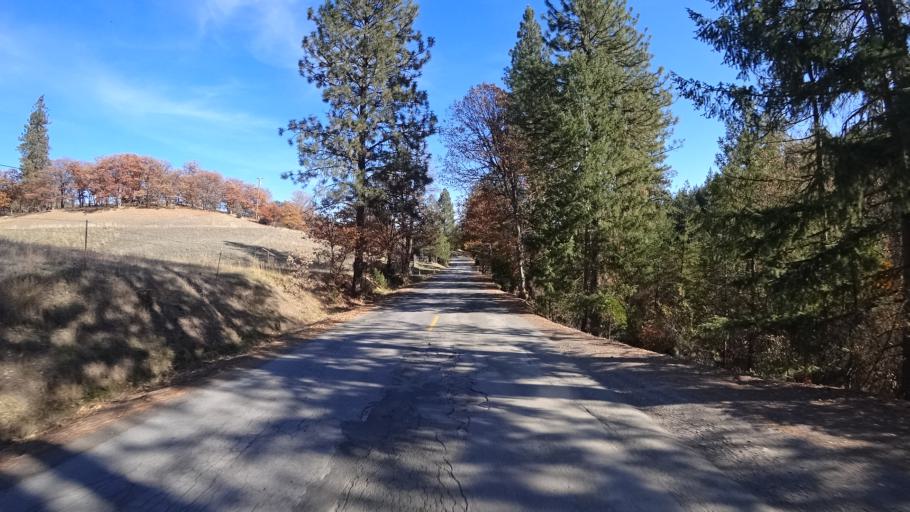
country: US
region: California
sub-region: Siskiyou County
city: Yreka
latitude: 41.7227
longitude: -122.6954
